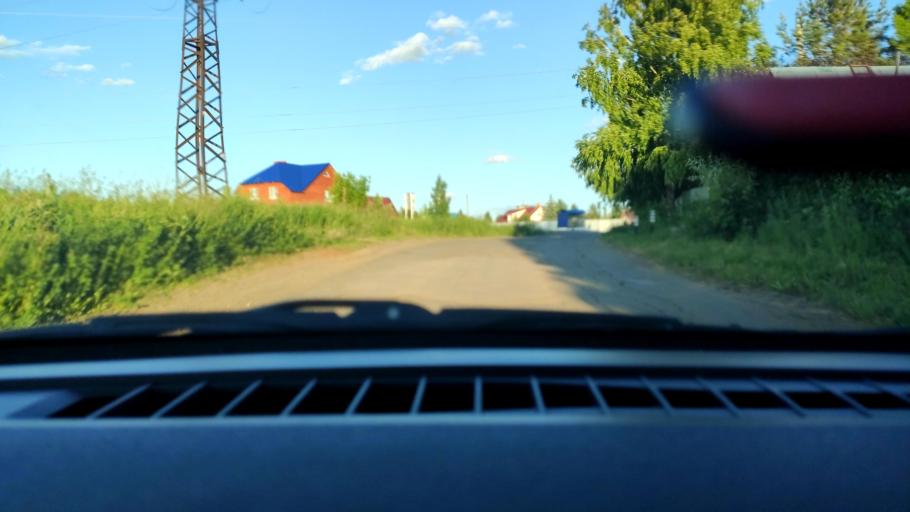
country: RU
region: Perm
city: Kultayevo
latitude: 57.9362
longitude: 55.8641
